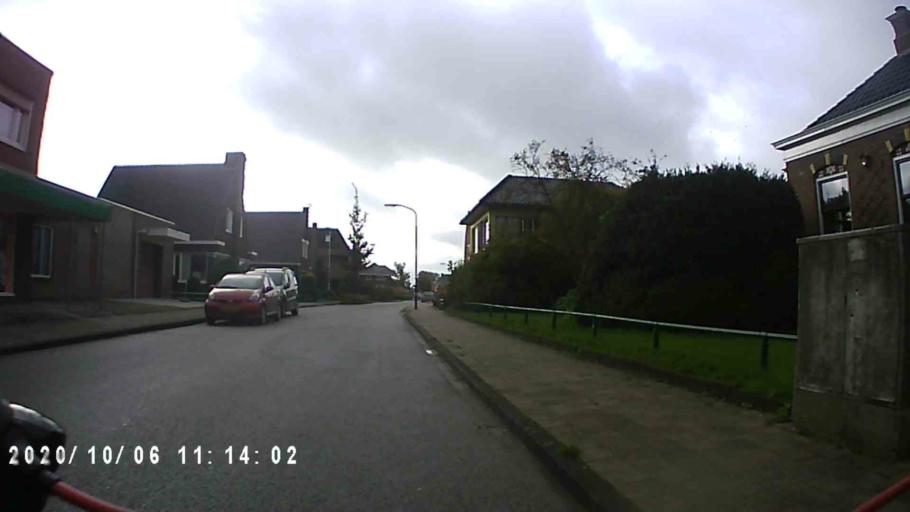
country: NL
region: Groningen
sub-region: Gemeente De Marne
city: Ulrum
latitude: 53.3609
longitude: 6.3767
